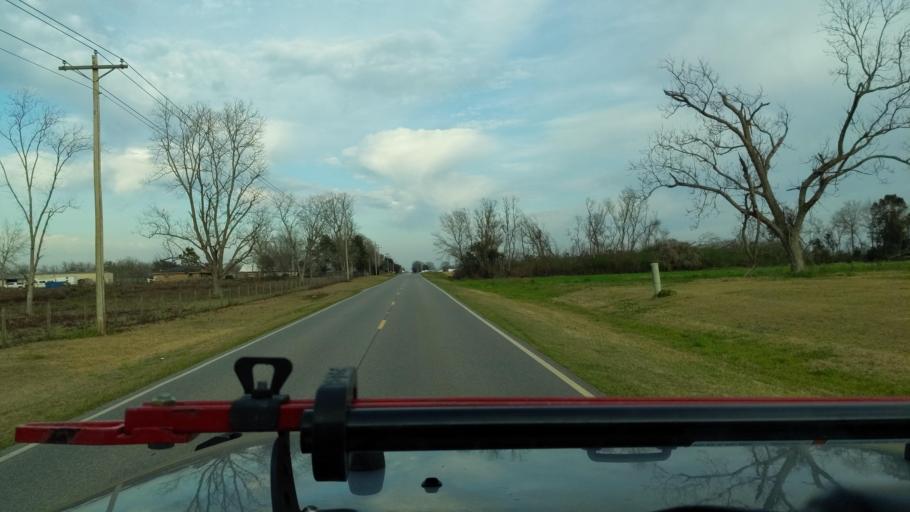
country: US
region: Alabama
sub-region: Baldwin County
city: Foley
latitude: 30.4580
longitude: -87.7229
